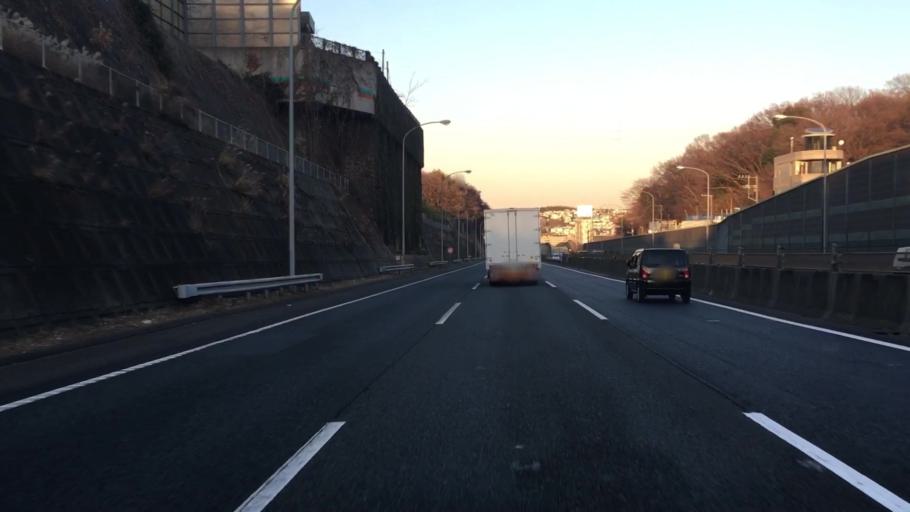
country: JP
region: Kanagawa
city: Yokohama
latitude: 35.4572
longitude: 139.5837
